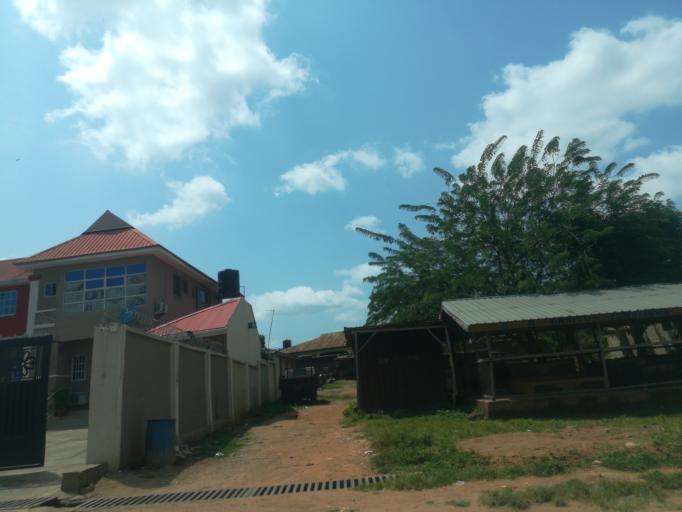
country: NG
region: Oyo
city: Moniya
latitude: 7.5427
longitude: 3.9110
